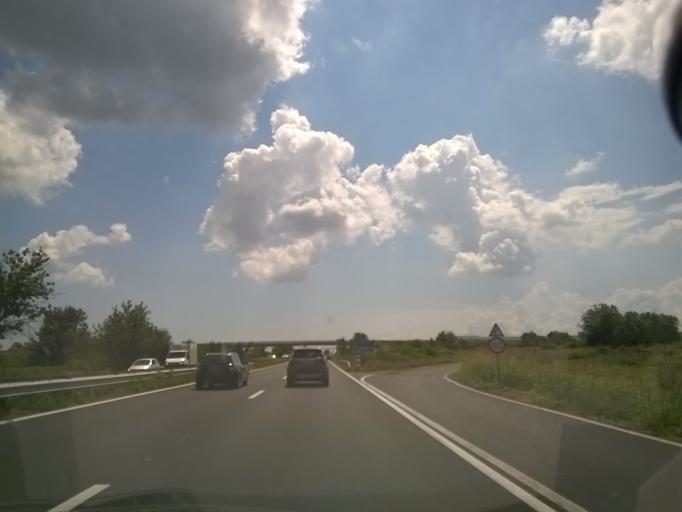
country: BG
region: Burgas
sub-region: Obshtina Burgas
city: Burgas
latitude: 42.5777
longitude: 27.4082
